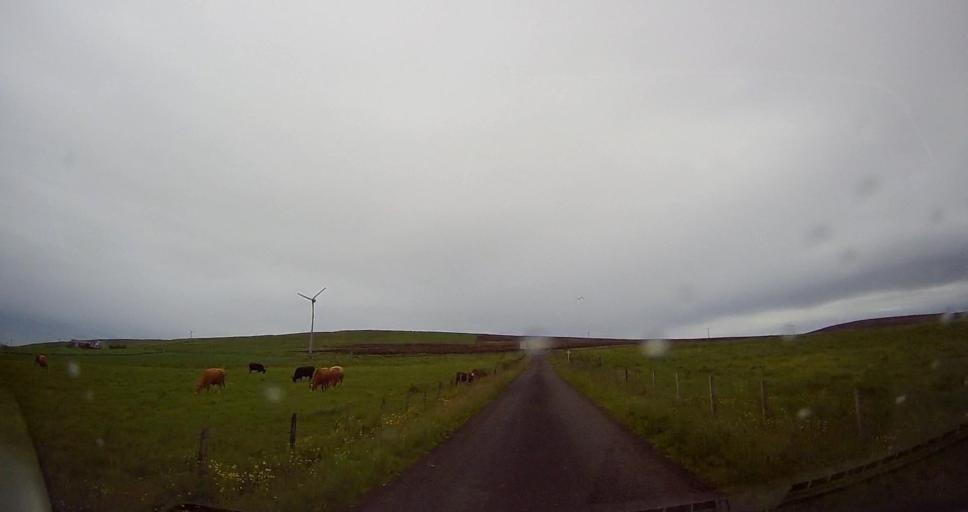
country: GB
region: Scotland
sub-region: Orkney Islands
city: Stromness
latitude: 59.0905
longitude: -3.1828
